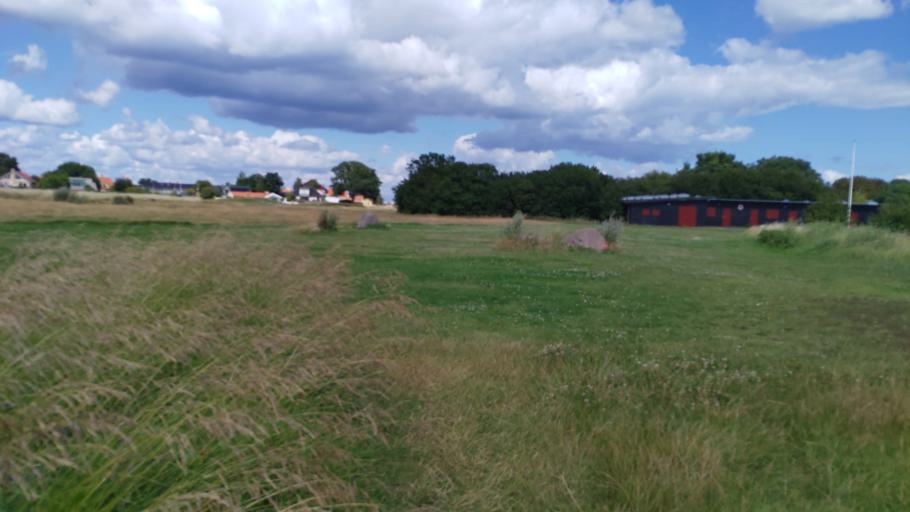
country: DK
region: Capital Region
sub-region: Dragor Kommune
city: Dragor
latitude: 55.5871
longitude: 12.6719
